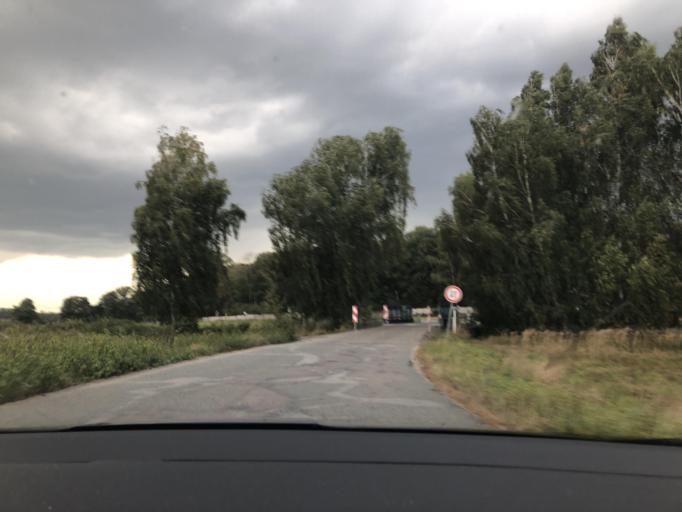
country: CZ
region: Pardubicky
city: Chvaletice
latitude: 50.0517
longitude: 15.3973
